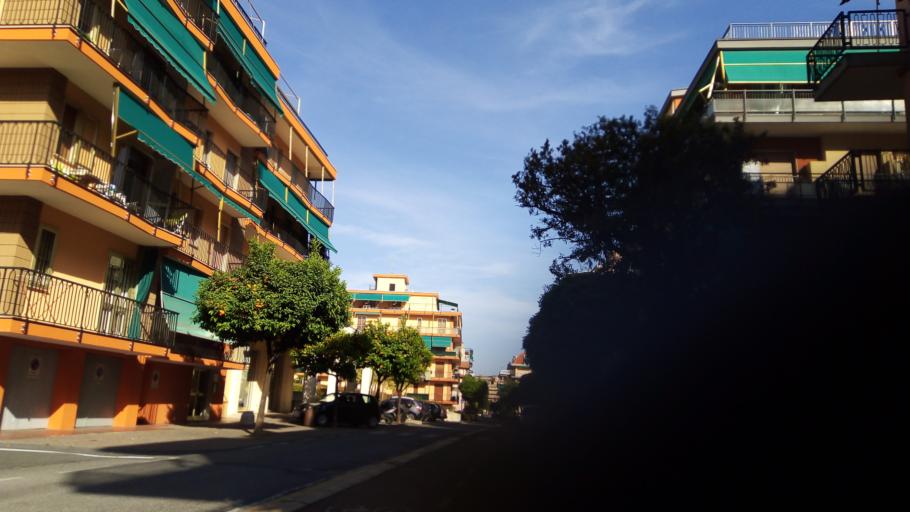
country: IT
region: Liguria
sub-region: Provincia di Savona
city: Borghetto Santo Spirito
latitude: 44.1126
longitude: 8.2387
